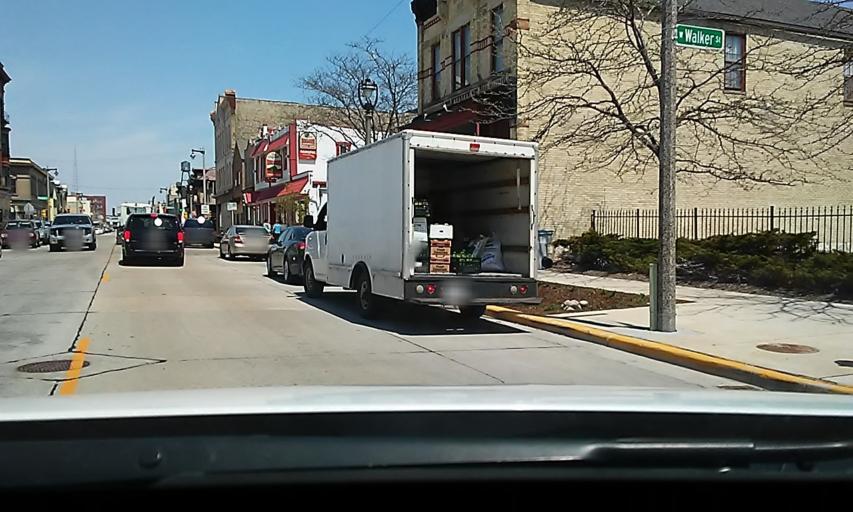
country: US
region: Wisconsin
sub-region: Milwaukee County
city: Milwaukee
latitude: 43.0223
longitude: -87.9168
